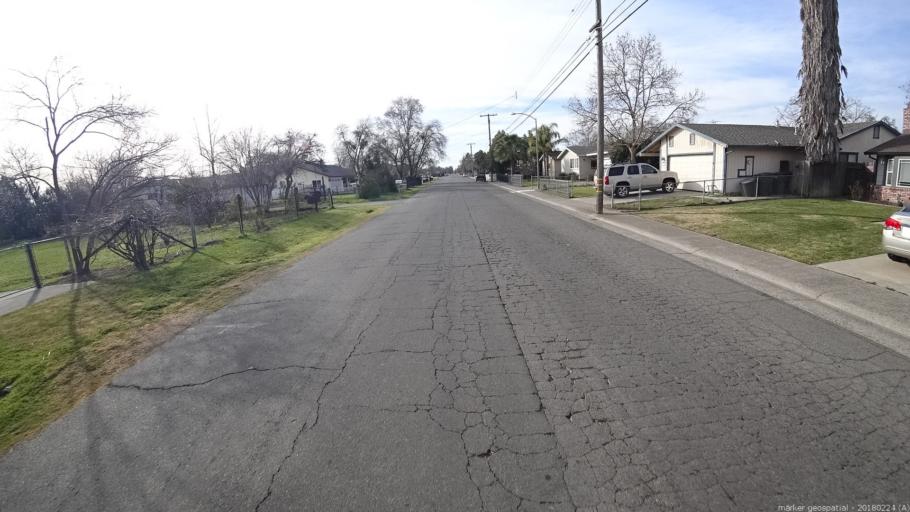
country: US
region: California
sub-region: Sacramento County
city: Rio Linda
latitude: 38.6897
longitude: -121.4615
